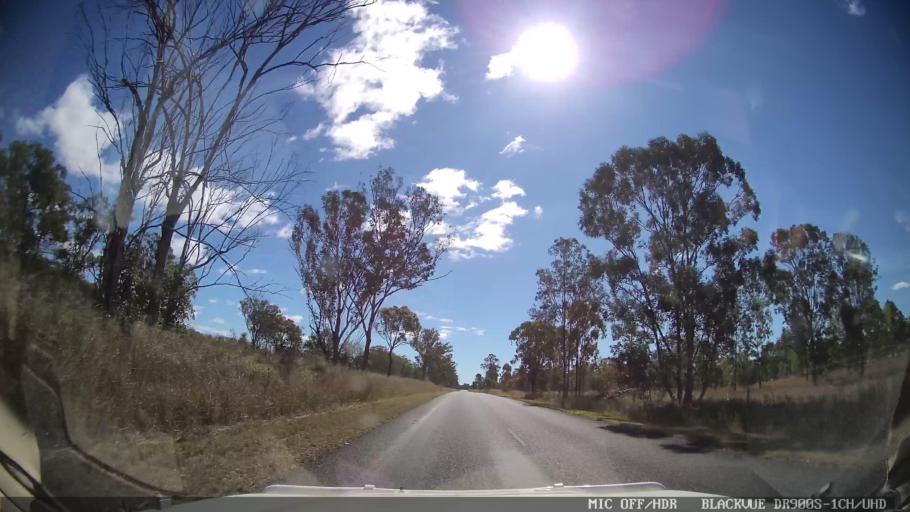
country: AU
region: Queensland
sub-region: Gladstone
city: Toolooa
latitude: -24.4451
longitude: 151.3425
